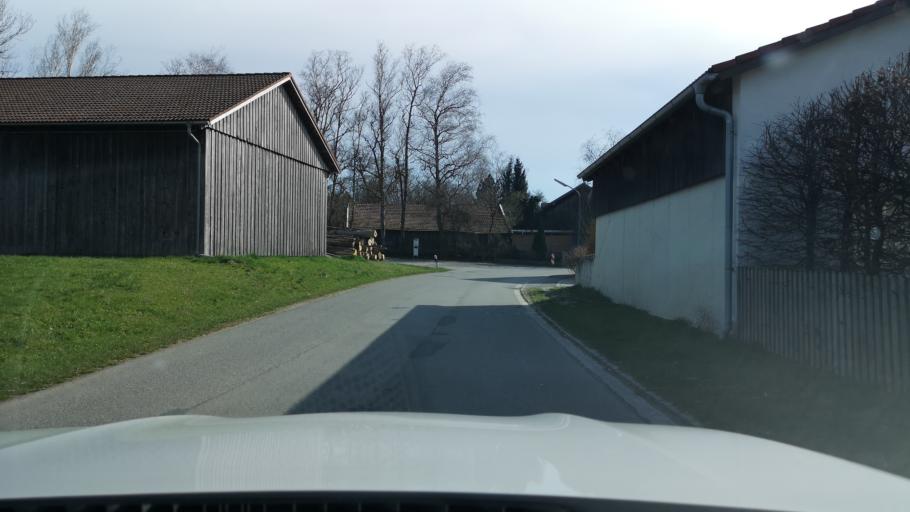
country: DE
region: Bavaria
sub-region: Upper Bavaria
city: Finsing
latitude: 48.2212
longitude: 11.8270
